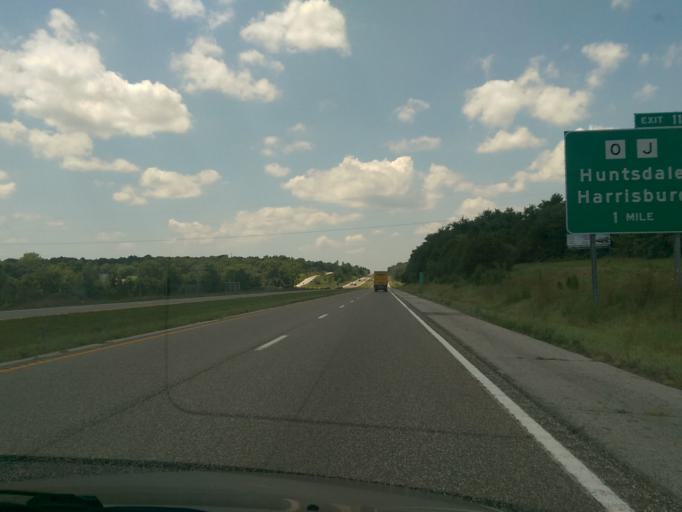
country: US
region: Missouri
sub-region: Boone County
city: Columbia
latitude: 38.9731
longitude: -92.4720
